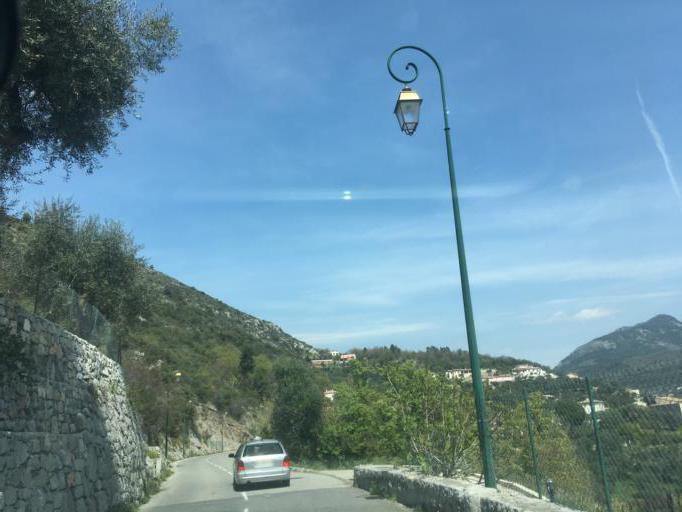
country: FR
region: Provence-Alpes-Cote d'Azur
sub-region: Departement des Alpes-Maritimes
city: Levens
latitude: 43.8427
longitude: 7.2149
